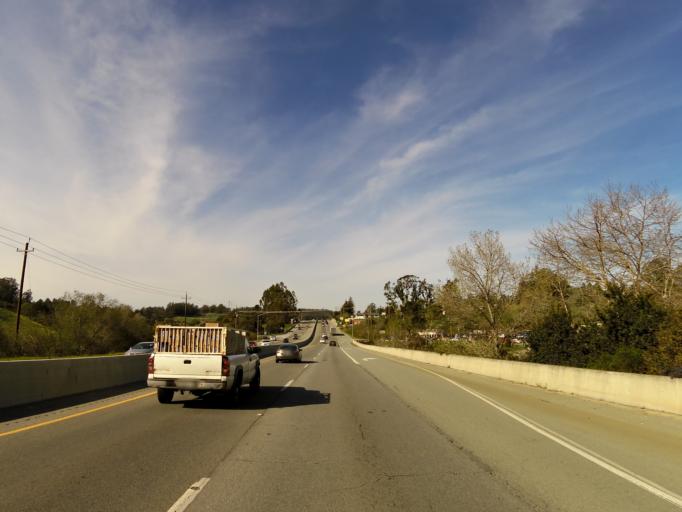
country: US
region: California
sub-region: Monterey County
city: Prunedale
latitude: 36.7707
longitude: -121.6690
